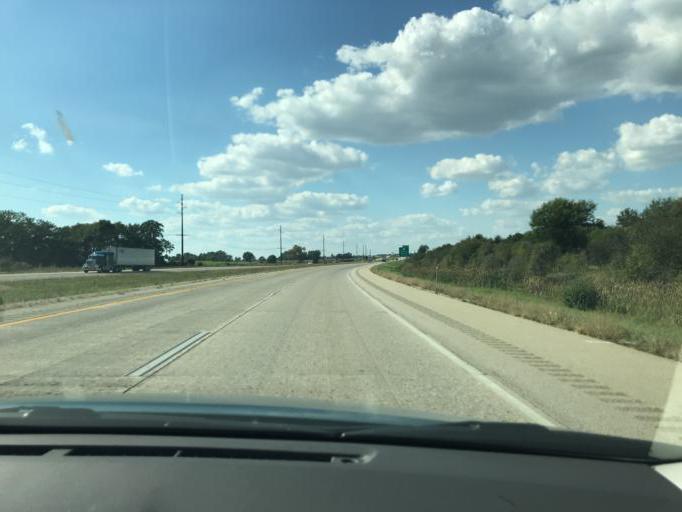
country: US
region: Wisconsin
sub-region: Walworth County
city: Delavan
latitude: 42.6130
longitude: -88.6513
